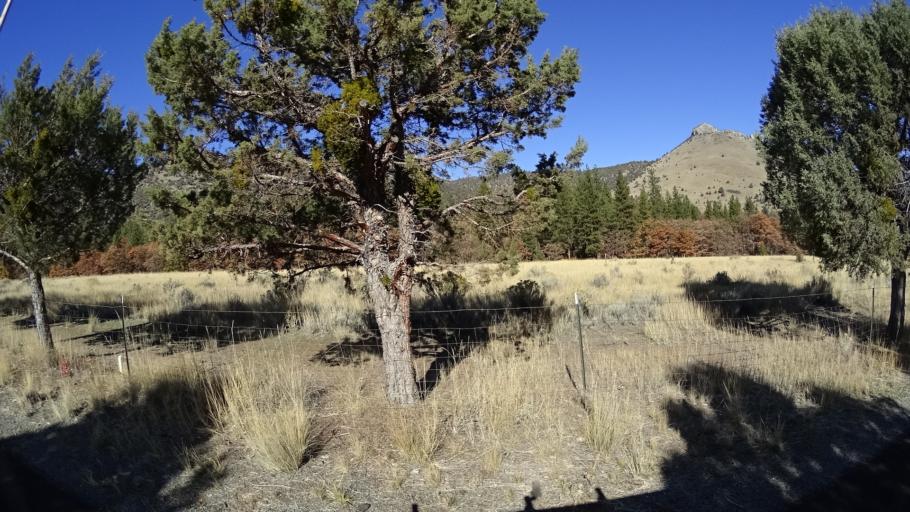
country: US
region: California
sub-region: Siskiyou County
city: Weed
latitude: 41.5034
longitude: -122.5848
